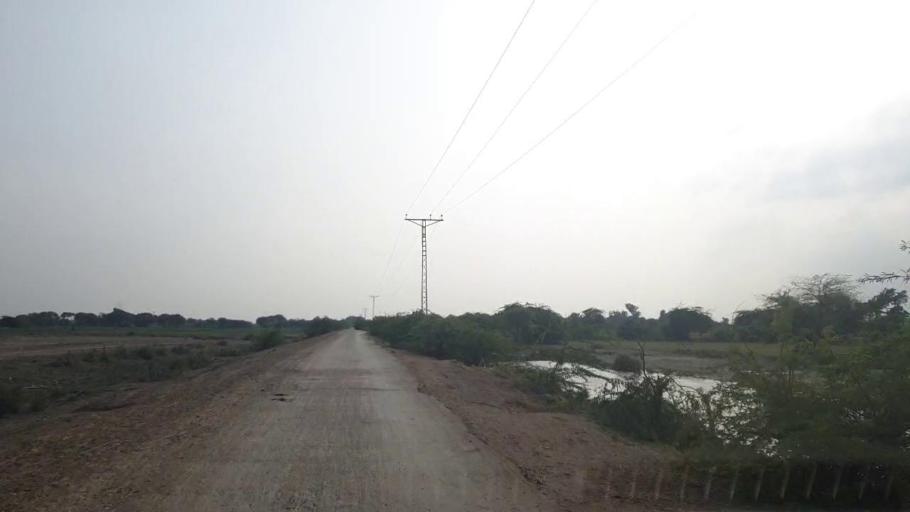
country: PK
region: Sindh
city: Badin
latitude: 24.6176
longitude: 68.6871
